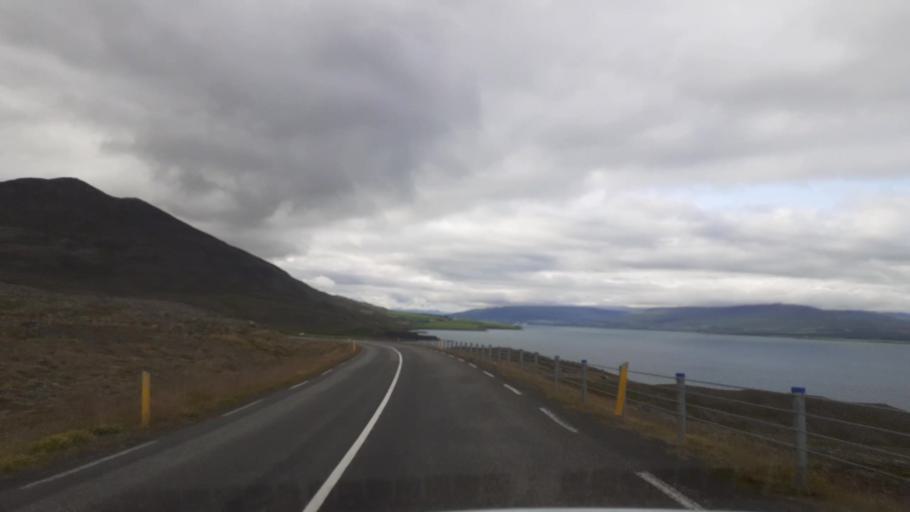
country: IS
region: Northeast
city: Akureyri
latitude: 65.8293
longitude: -18.0582
